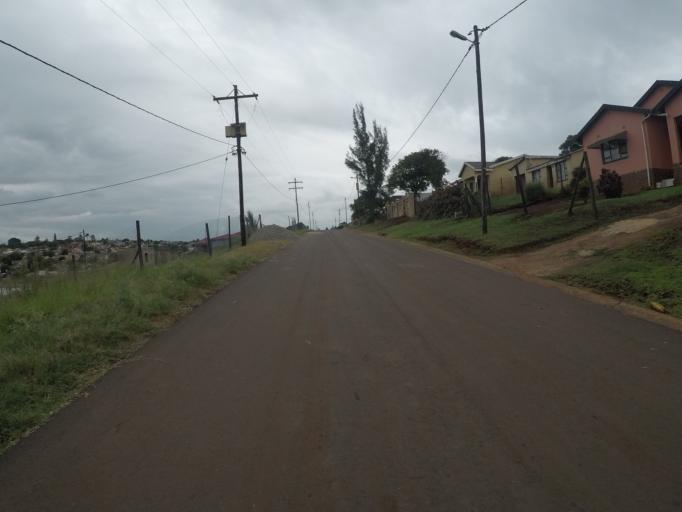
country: ZA
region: KwaZulu-Natal
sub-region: uThungulu District Municipality
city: Empangeni
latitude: -28.7756
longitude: 31.8566
